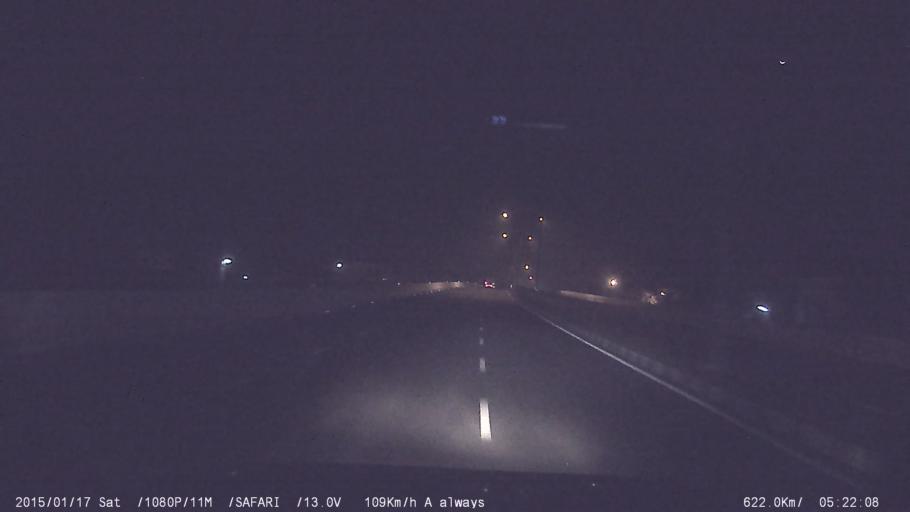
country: IN
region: Tamil Nadu
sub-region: Vellore
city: Katpadi
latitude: 12.9420
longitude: 79.1835
